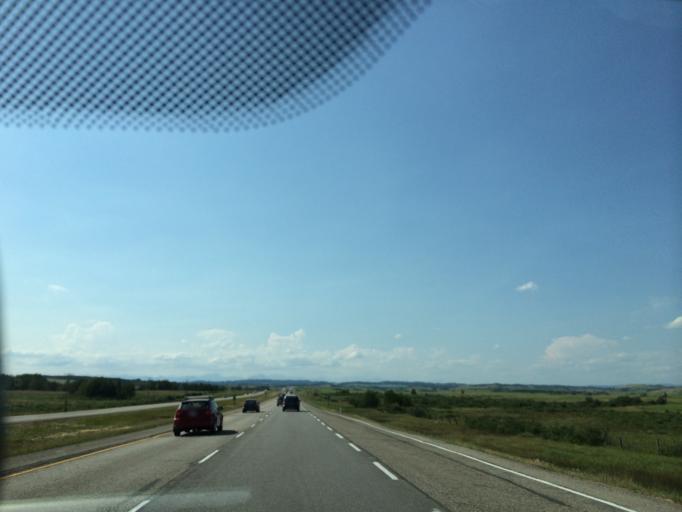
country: CA
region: Alberta
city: Cochrane
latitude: 51.1006
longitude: -114.6075
